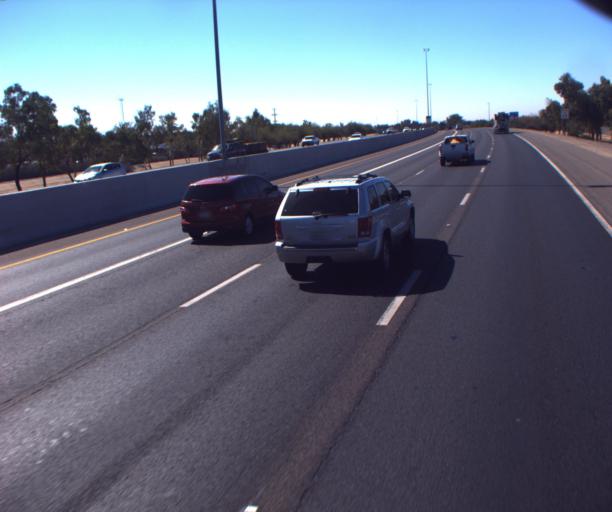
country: US
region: Arizona
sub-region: Maricopa County
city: Sun City
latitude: 33.6003
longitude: -112.2562
